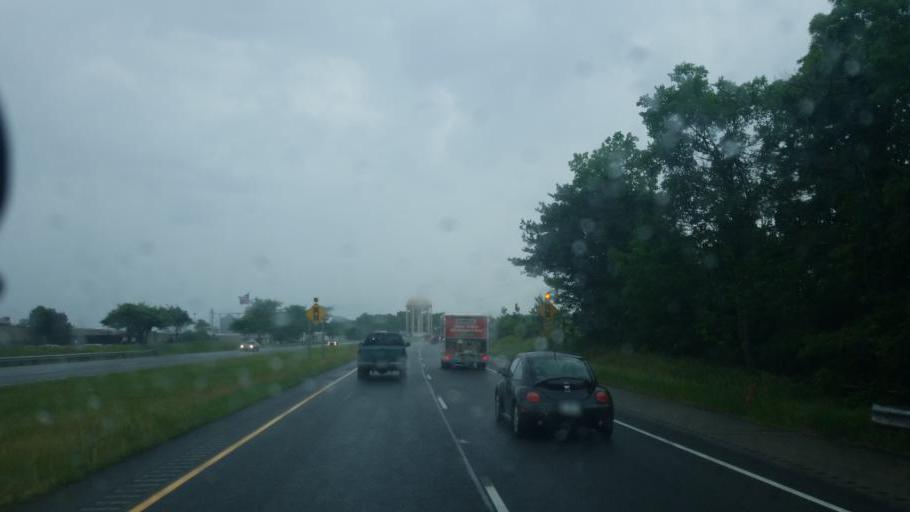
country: US
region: Indiana
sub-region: Whitley County
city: Churubusco
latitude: 41.1263
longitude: -85.3710
